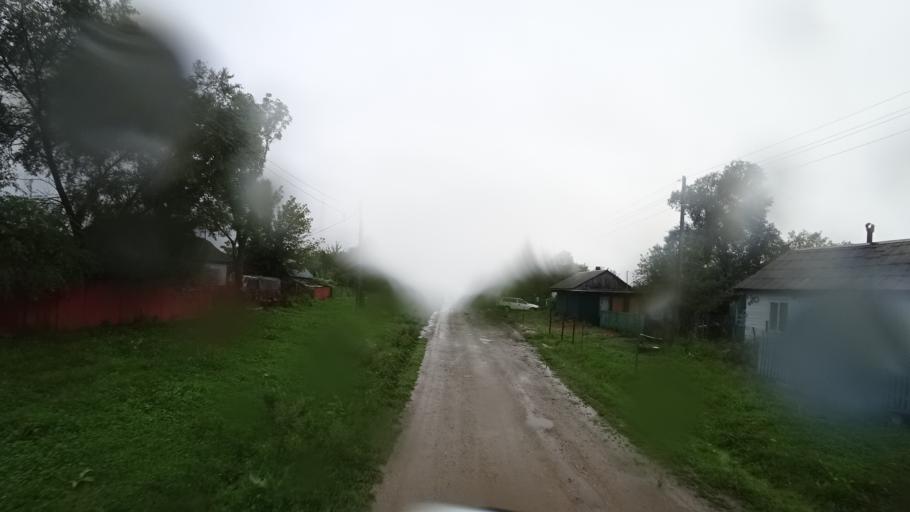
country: RU
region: Primorskiy
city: Monastyrishche
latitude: 44.2521
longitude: 132.4262
